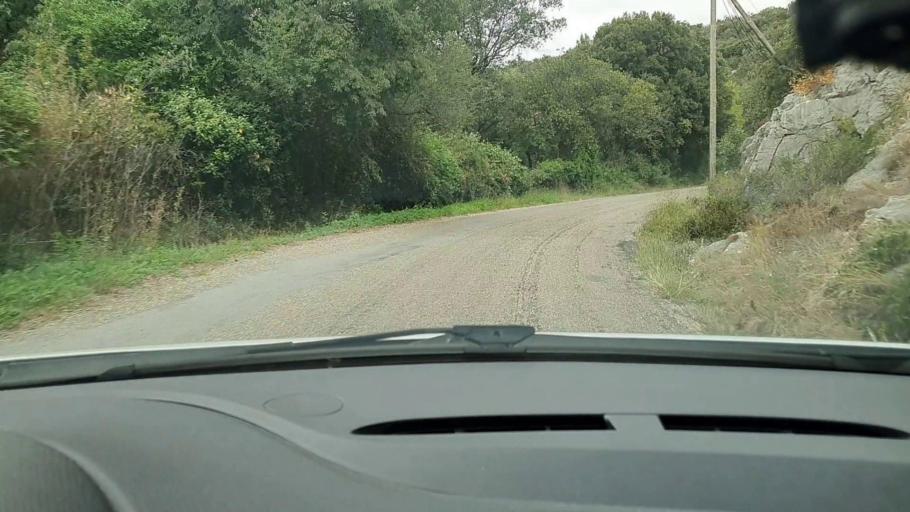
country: FR
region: Languedoc-Roussillon
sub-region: Departement du Gard
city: Montaren-et-Saint-Mediers
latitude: 44.0605
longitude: 4.3200
